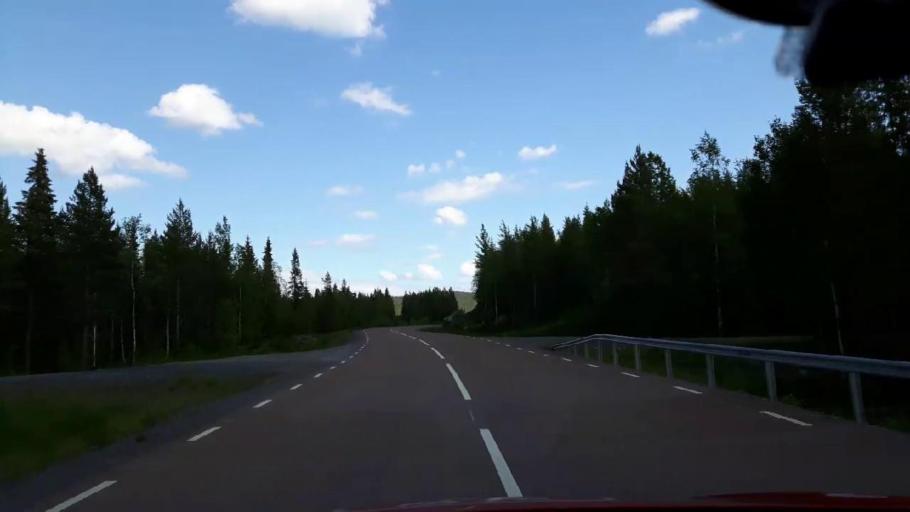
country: SE
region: Jaemtland
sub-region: Krokoms Kommun
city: Valla
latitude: 64.0485
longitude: 14.1736
